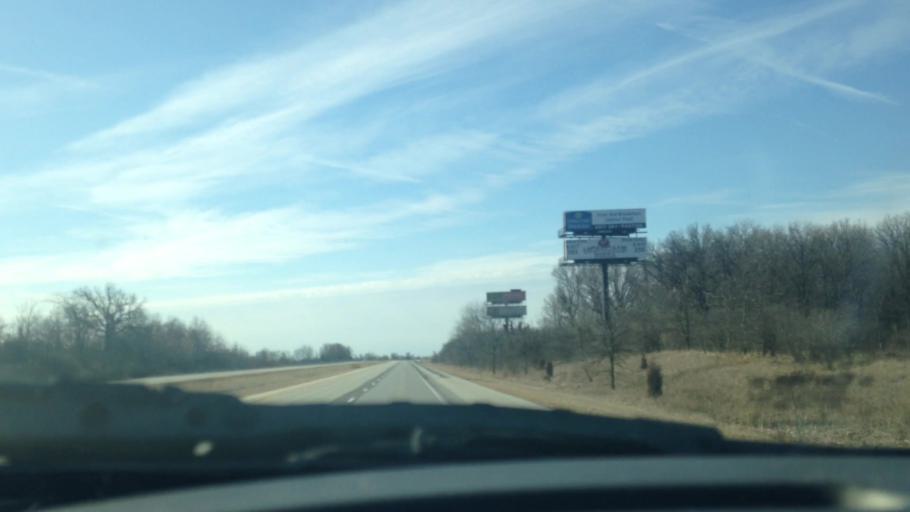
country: US
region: Illinois
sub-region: Ford County
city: Paxton
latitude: 40.5151
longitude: -88.0848
